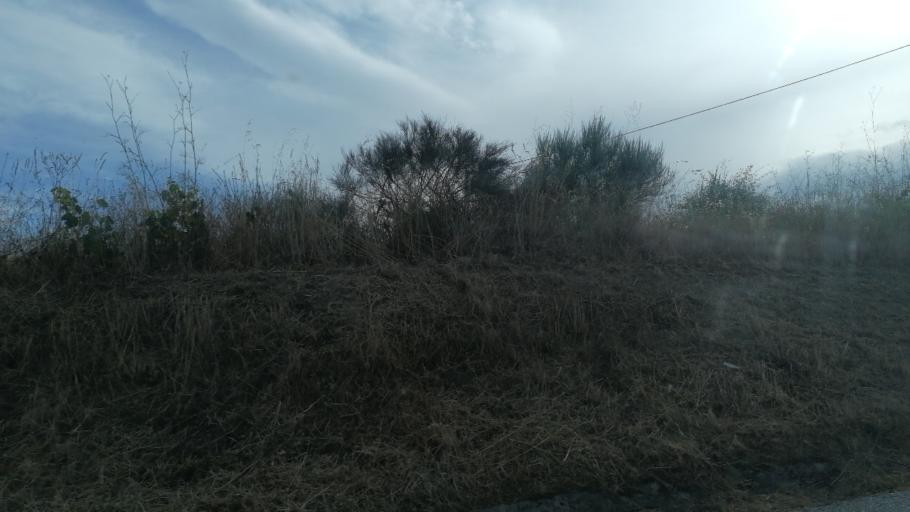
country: PT
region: Viseu
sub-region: Sao Joao da Pesqueira
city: Sao Joao da Pesqueira
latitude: 41.1039
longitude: -7.3854
